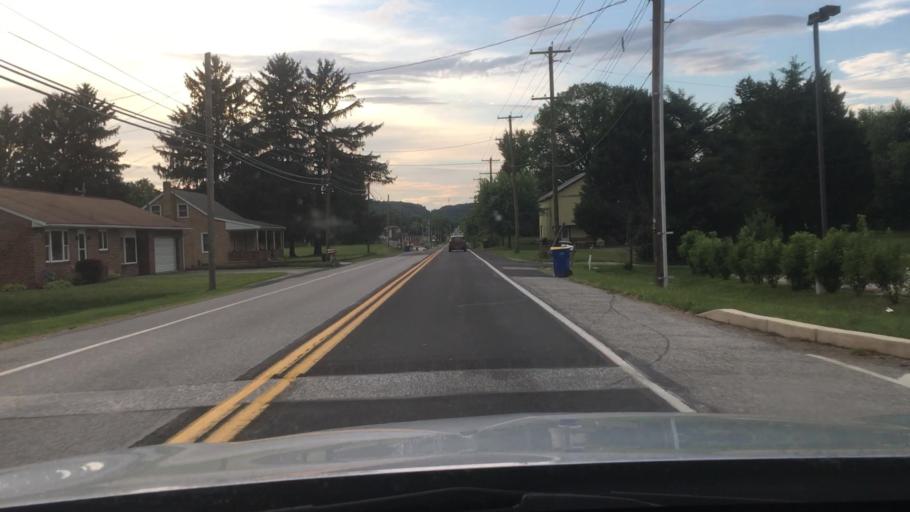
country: US
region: Pennsylvania
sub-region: York County
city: Dover
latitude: 40.0091
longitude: -76.8581
